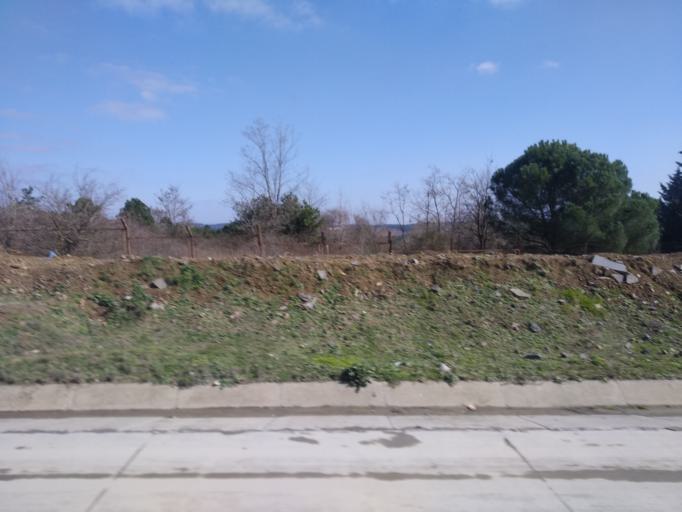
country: TR
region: Istanbul
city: Kemerburgaz
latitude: 41.1250
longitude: 28.9456
